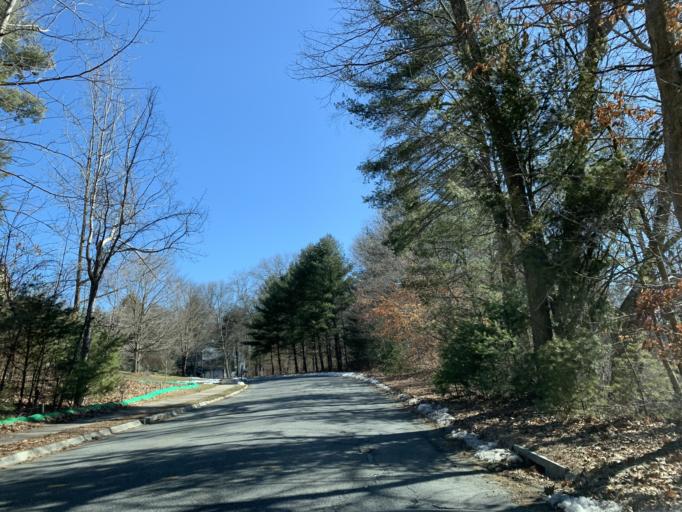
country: US
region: Massachusetts
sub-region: Bristol County
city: Norton
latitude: 41.9443
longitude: -71.1911
